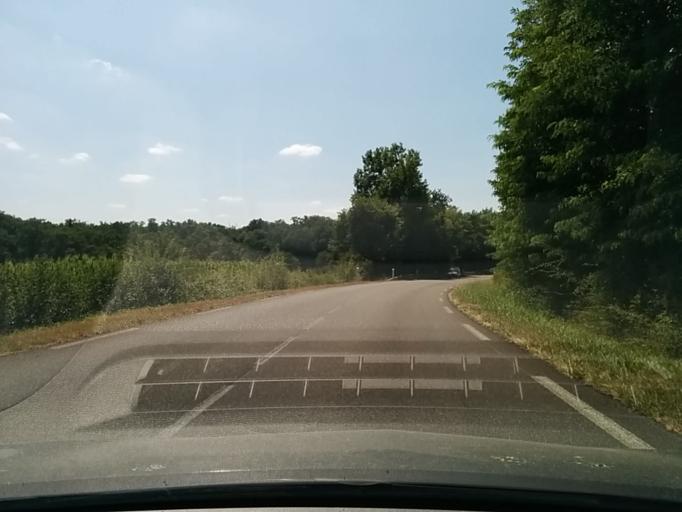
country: FR
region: Midi-Pyrenees
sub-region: Departement du Gers
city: Nogaro
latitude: 43.7489
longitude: -0.0776
